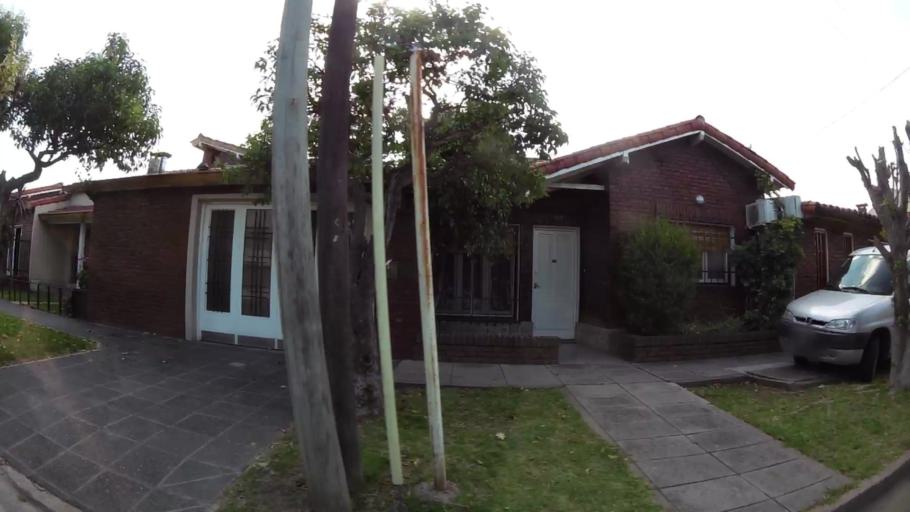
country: AR
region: Buenos Aires
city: San Justo
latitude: -34.6689
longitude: -58.5857
